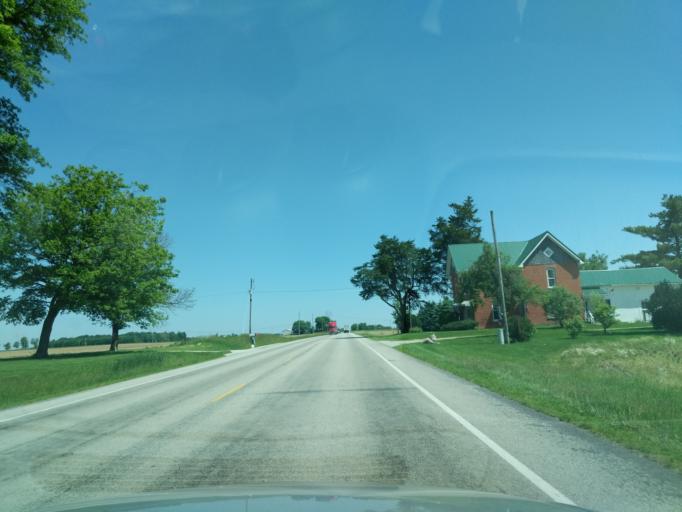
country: US
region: Indiana
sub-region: Huntington County
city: Huntington
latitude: 40.9267
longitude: -85.4709
